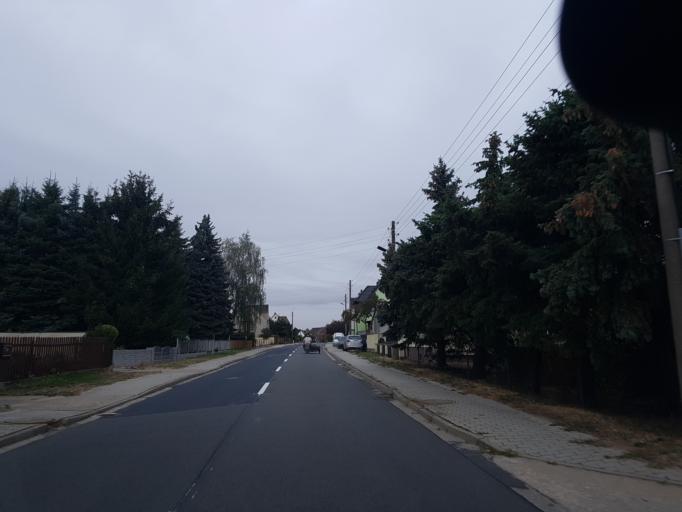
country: DE
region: Saxony-Anhalt
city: Prettin
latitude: 51.6568
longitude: 12.9397
